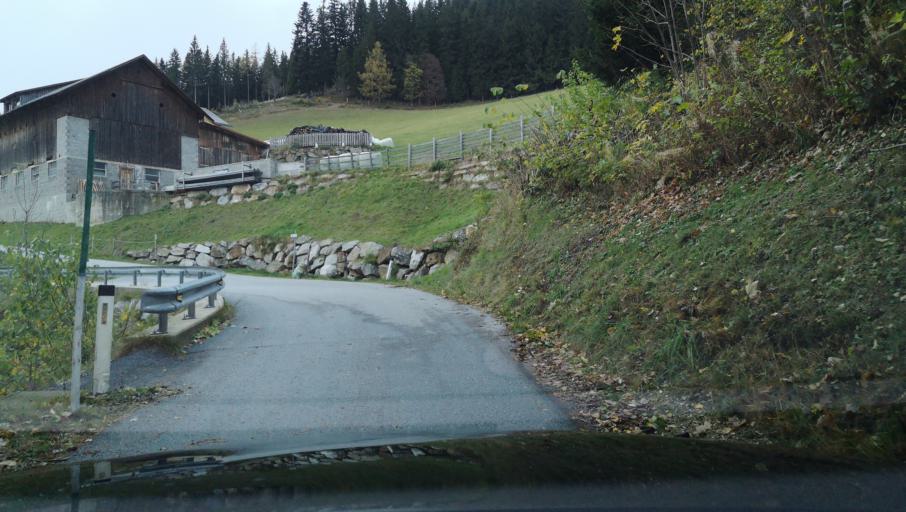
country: AT
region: Styria
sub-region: Politischer Bezirk Weiz
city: Gasen
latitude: 47.3598
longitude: 15.6049
